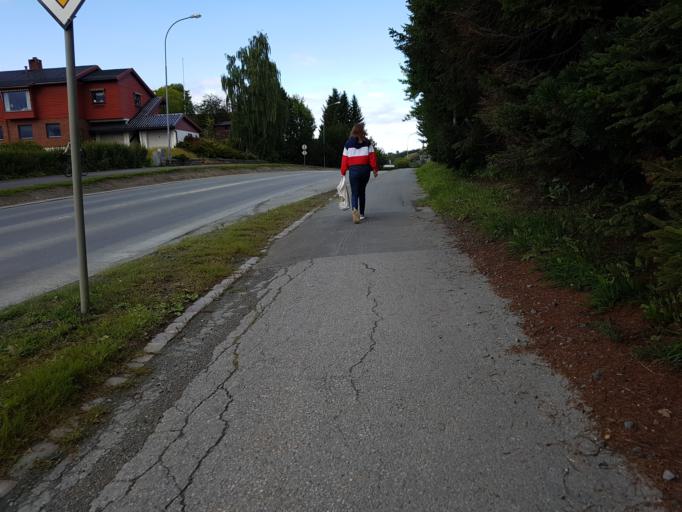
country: NO
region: Sor-Trondelag
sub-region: Trondheim
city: Trondheim
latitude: 63.4003
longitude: 10.4228
